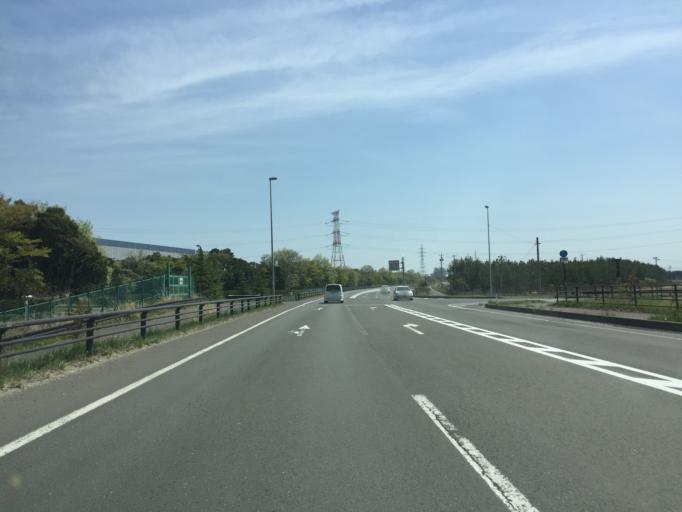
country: JP
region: Miyagi
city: Marumori
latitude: 37.8453
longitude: 140.9351
